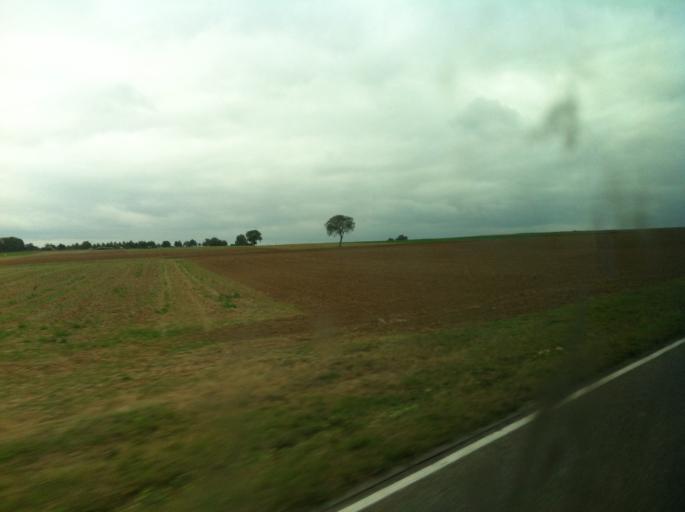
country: DE
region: Rheinland-Pfalz
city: Ober-Olm
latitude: 49.9471
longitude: 8.1830
